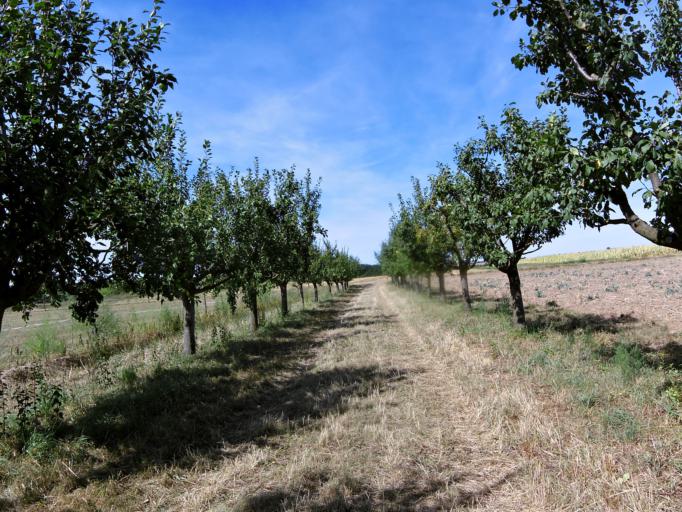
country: DE
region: Bavaria
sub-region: Regierungsbezirk Unterfranken
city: Eibelstadt
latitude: 49.7474
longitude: 10.0079
